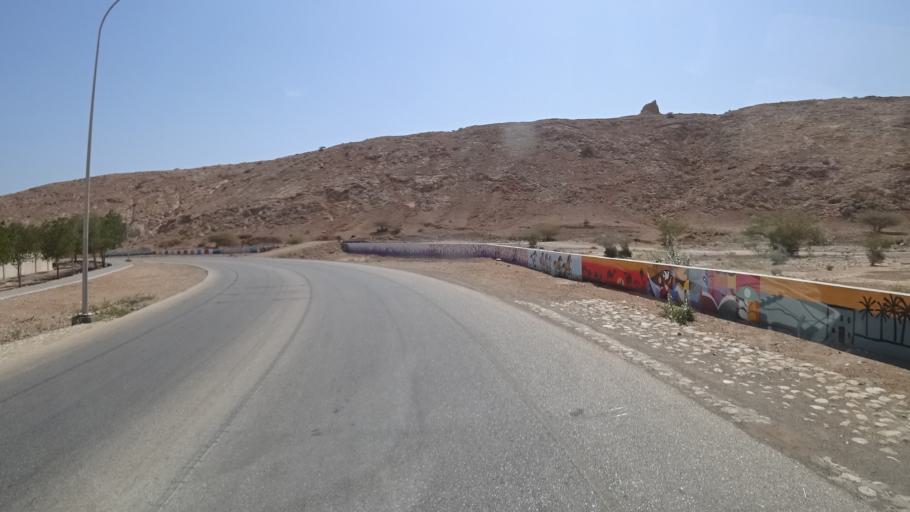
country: OM
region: Ash Sharqiyah
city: Sur
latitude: 22.5622
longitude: 59.5461
